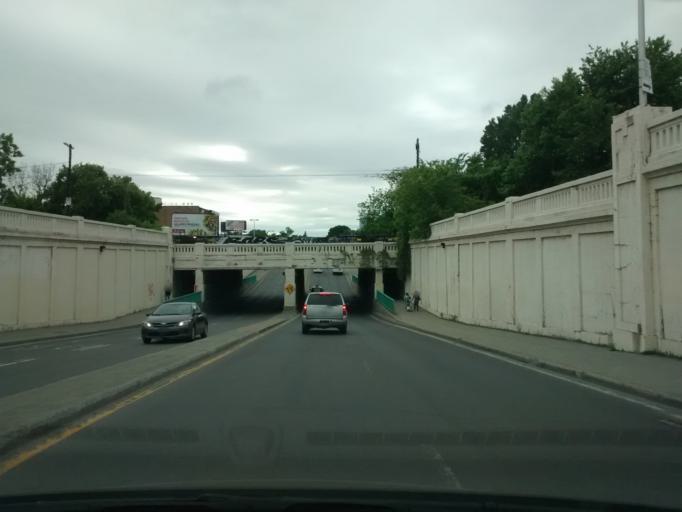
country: CA
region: Quebec
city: Mont-Royal
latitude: 45.5041
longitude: -73.6394
